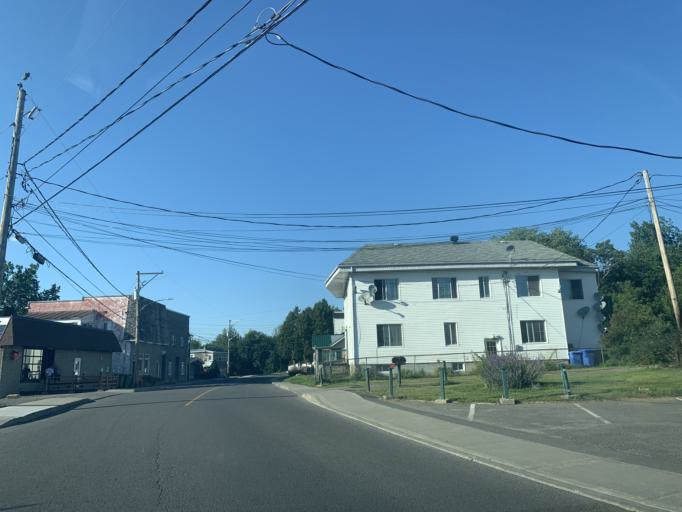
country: CA
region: Ontario
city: Hawkesbury
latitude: 45.6267
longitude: -74.6045
